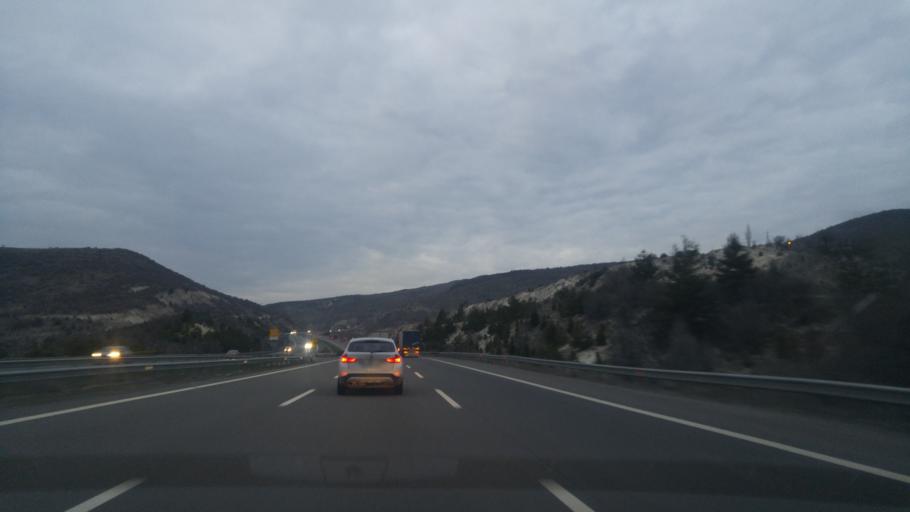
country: TR
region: Ankara
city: Pecenek
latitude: 40.4748
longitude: 32.3537
